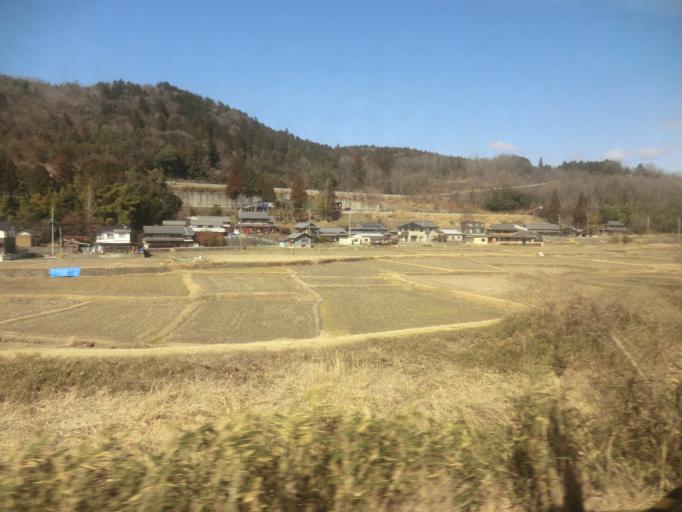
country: JP
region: Gifu
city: Mizunami
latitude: 35.4253
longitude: 137.3311
